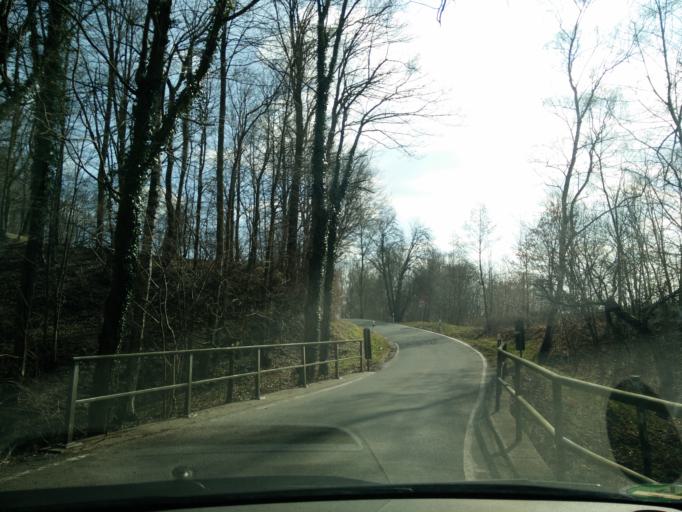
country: DE
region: Saxony
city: Zettlitz
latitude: 51.0918
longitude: 12.8128
